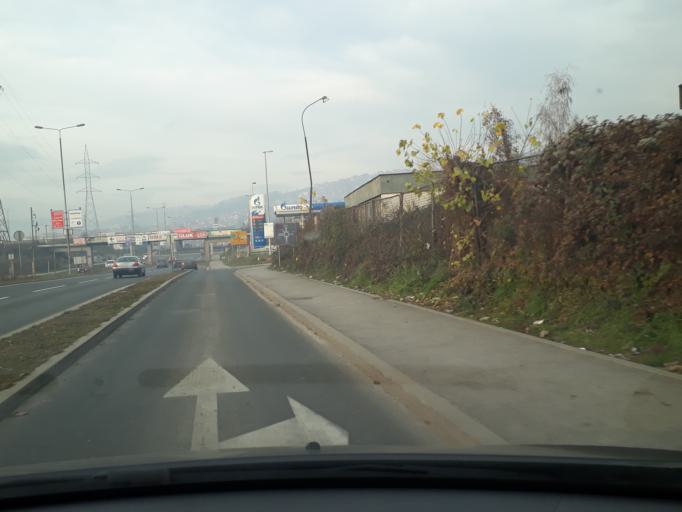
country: BA
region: Federation of Bosnia and Herzegovina
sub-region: Kanton Sarajevo
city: Sarajevo
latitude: 43.8490
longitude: 18.3271
